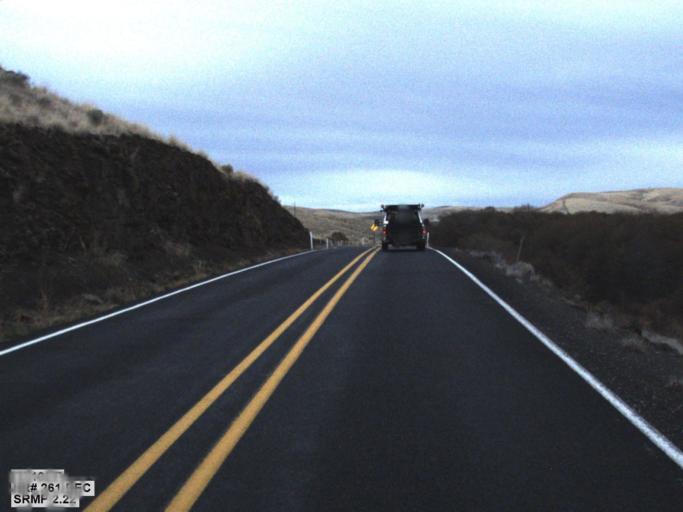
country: US
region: Washington
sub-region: Columbia County
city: Dayton
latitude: 46.5062
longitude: -118.0130
